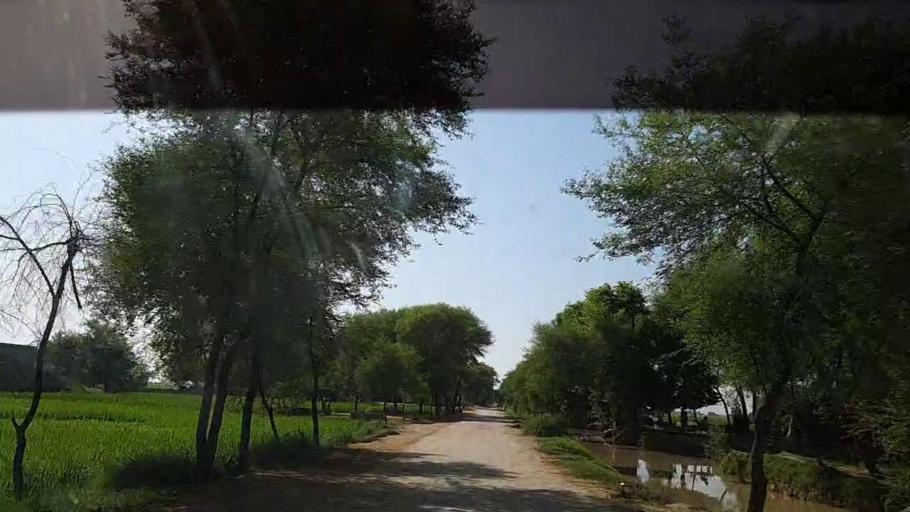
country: PK
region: Sindh
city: Ghauspur
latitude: 28.1753
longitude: 69.0480
